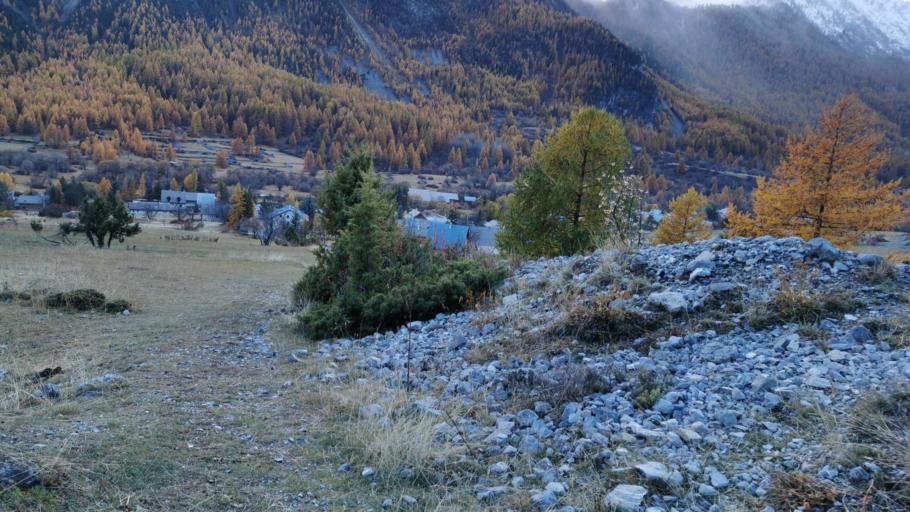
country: FR
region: Provence-Alpes-Cote d'Azur
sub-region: Departement des Hautes-Alpes
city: Villeneuve
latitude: 45.0220
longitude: 6.6193
